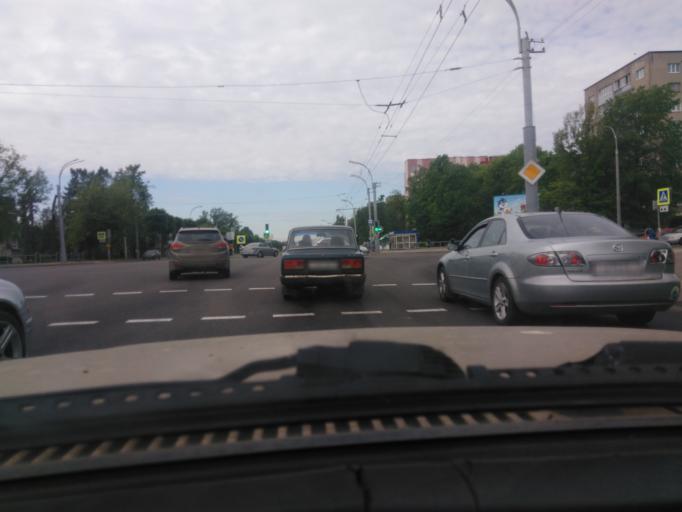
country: BY
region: Mogilev
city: Mahilyow
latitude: 53.9091
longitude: 30.3121
